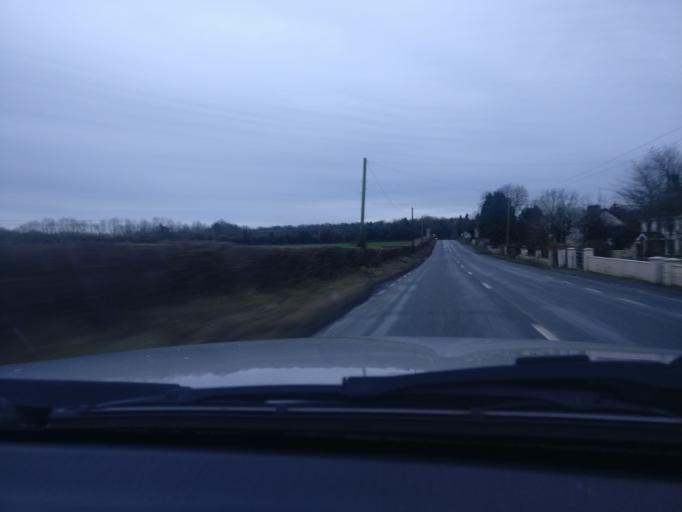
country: IE
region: Leinster
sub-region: An Mhi
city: Navan
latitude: 53.6628
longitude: -6.7252
